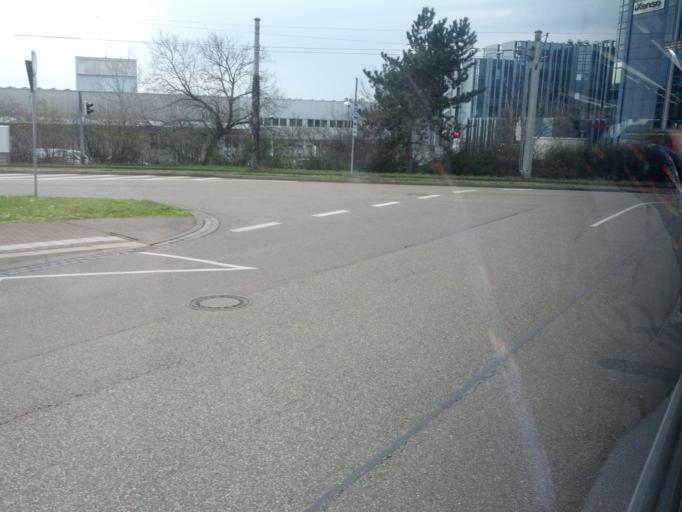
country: DE
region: Baden-Wuerttemberg
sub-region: Freiburg Region
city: Ebringen
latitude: 47.9880
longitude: 7.7960
